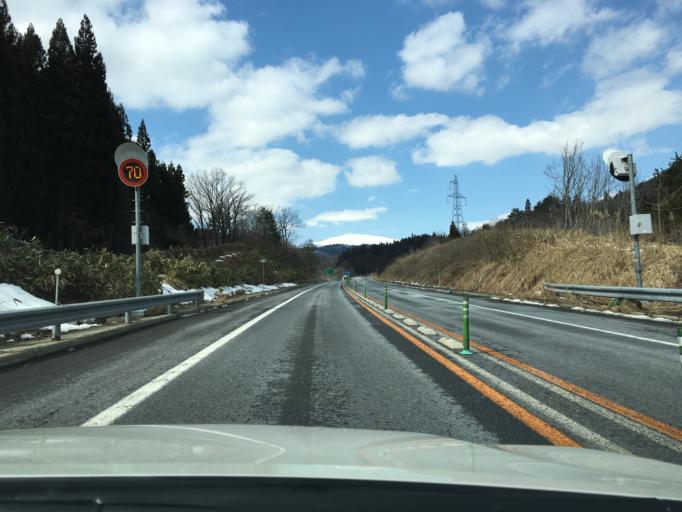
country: JP
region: Yamagata
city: Sagae
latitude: 38.4301
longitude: 140.1482
